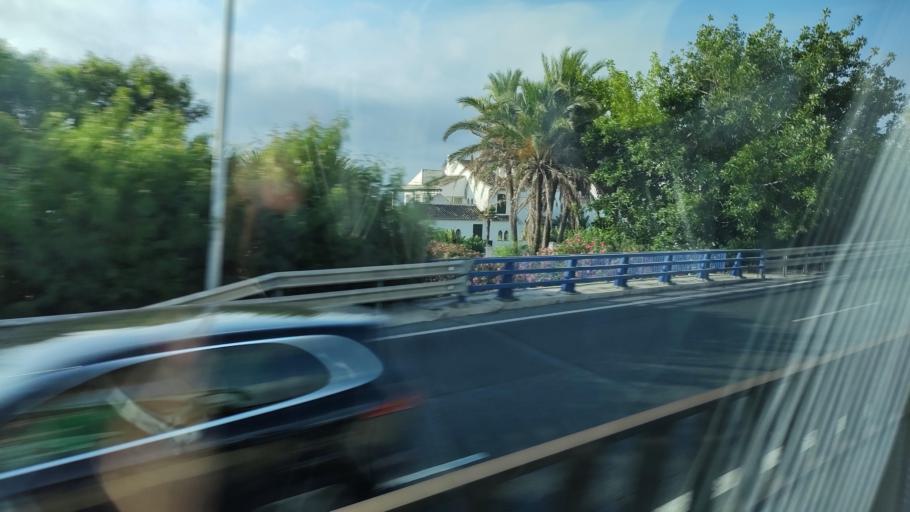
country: ES
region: Andalusia
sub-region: Provincia de Malaga
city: Fuengirola
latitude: 36.4958
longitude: -4.6901
